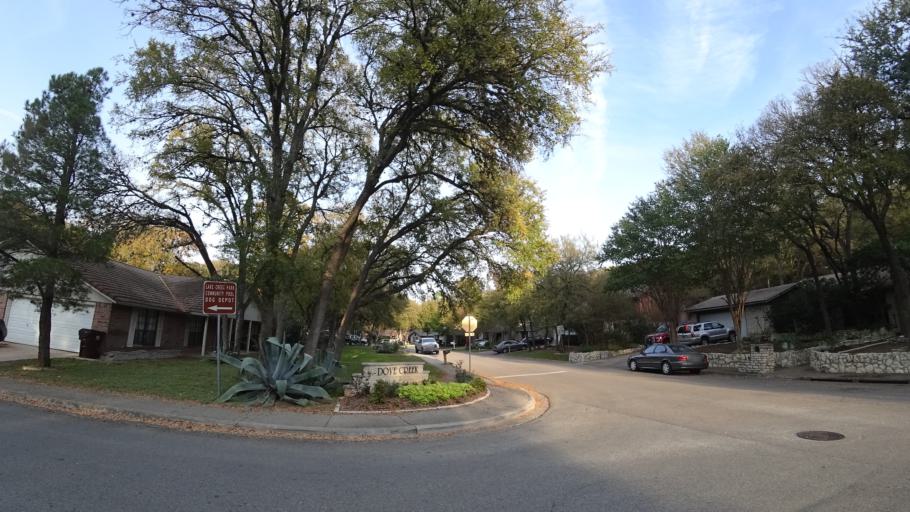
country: US
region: Texas
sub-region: Williamson County
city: Round Rock
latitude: 30.5057
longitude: -97.6739
